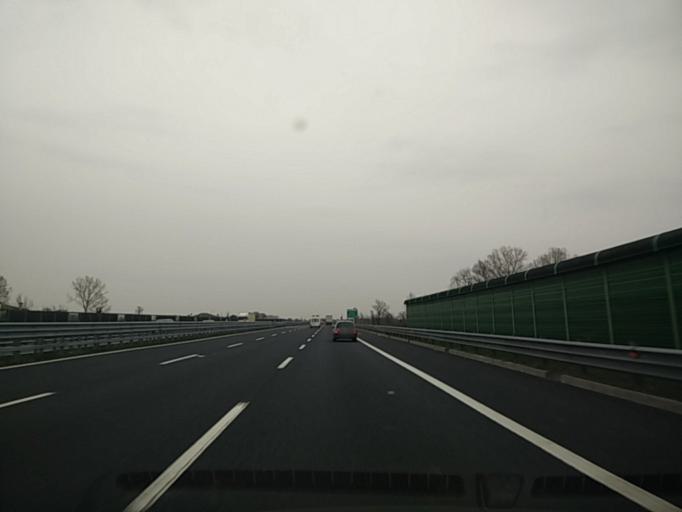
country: IT
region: Veneto
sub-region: Provincia di Venezia
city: Peseggia-Gardigiano
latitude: 45.5823
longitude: 12.1846
